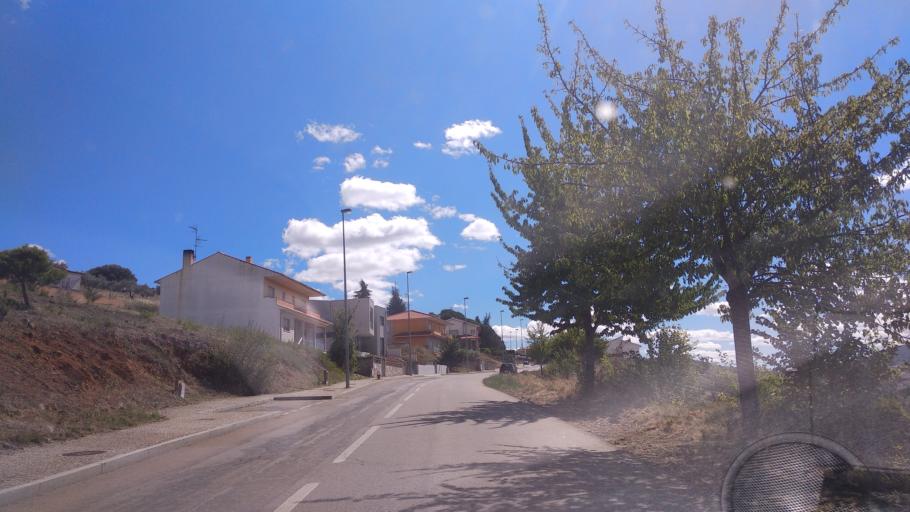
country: PT
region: Braganca
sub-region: Braganca Municipality
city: Braganca
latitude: 41.7916
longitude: -6.7672
